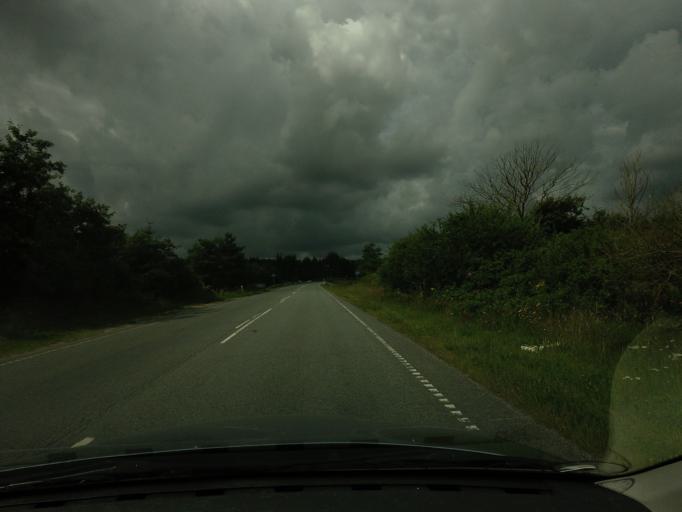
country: DK
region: North Denmark
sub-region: Hjorring Kommune
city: Hjorring
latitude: 57.4230
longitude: 9.9961
